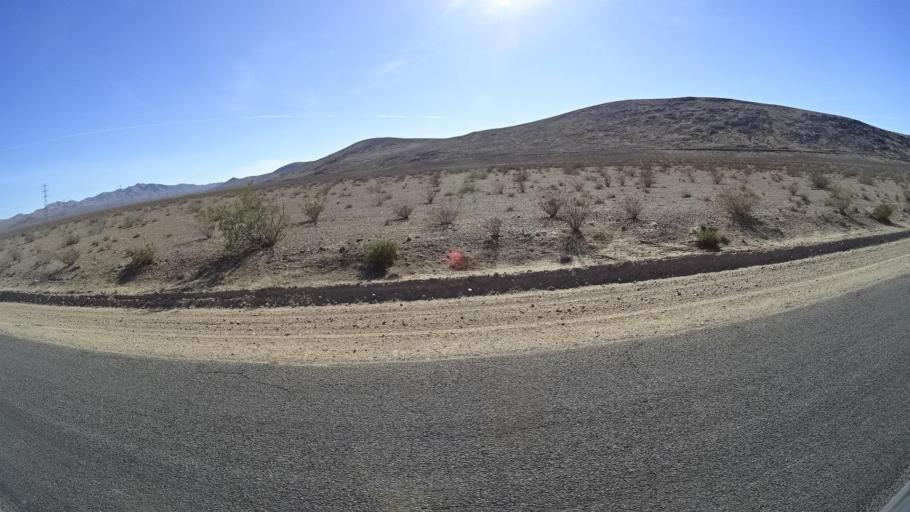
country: US
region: California
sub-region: Kern County
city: China Lake Acres
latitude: 35.5599
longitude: -117.7634
